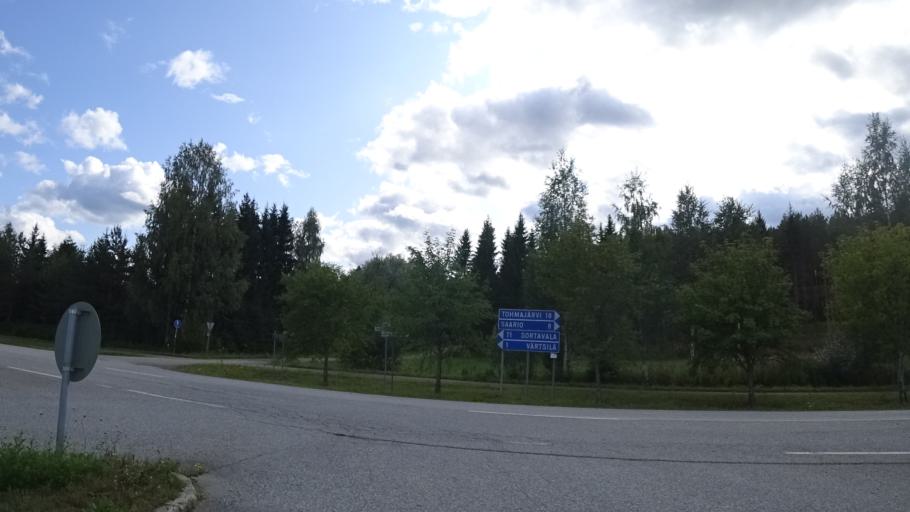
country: RU
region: Republic of Karelia
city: Vyartsilya
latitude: 62.2131
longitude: 30.5995
